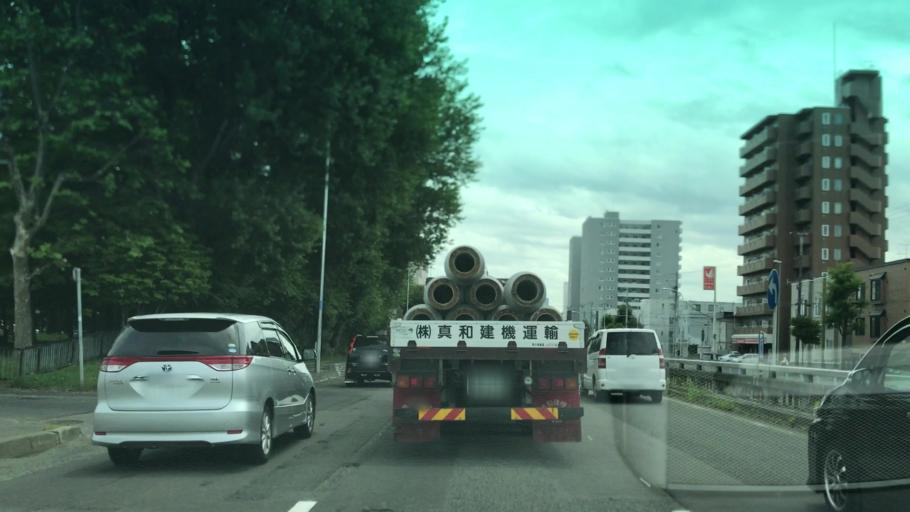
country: JP
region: Hokkaido
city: Sapporo
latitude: 43.0954
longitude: 141.3466
